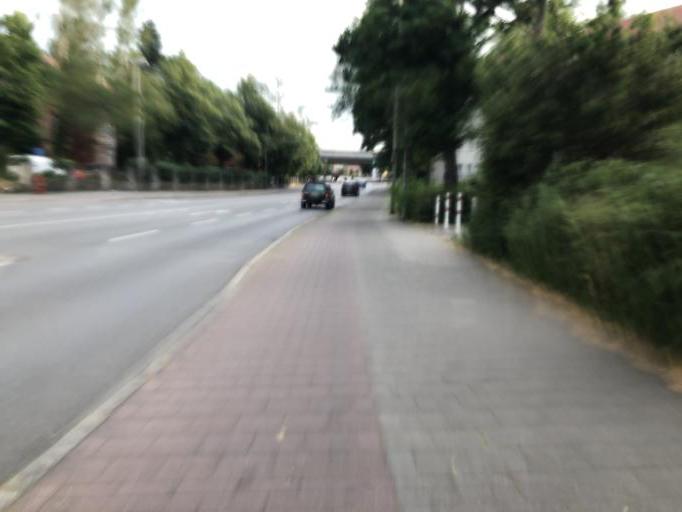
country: DE
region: Bavaria
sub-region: Regierungsbezirk Mittelfranken
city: Erlangen
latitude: 49.5919
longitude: 10.9989
